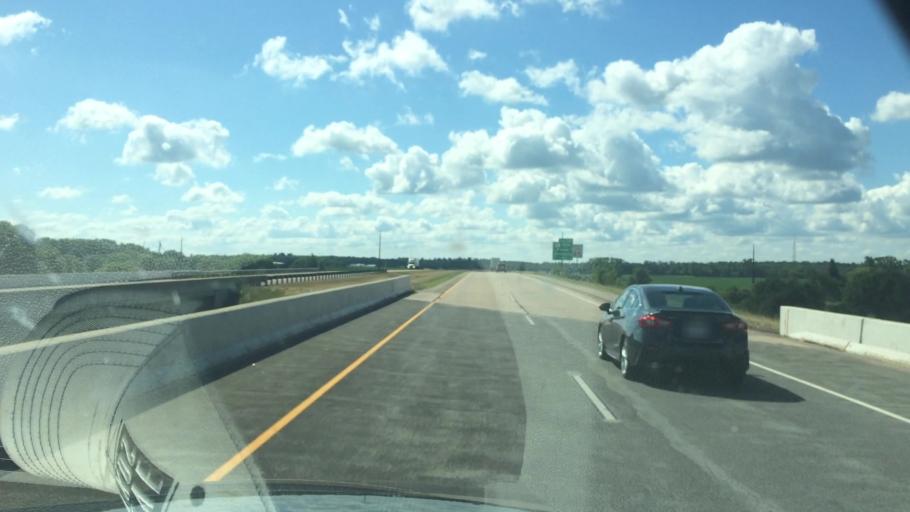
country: US
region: Wisconsin
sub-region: Portage County
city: Amherst
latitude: 44.4718
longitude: -89.3221
